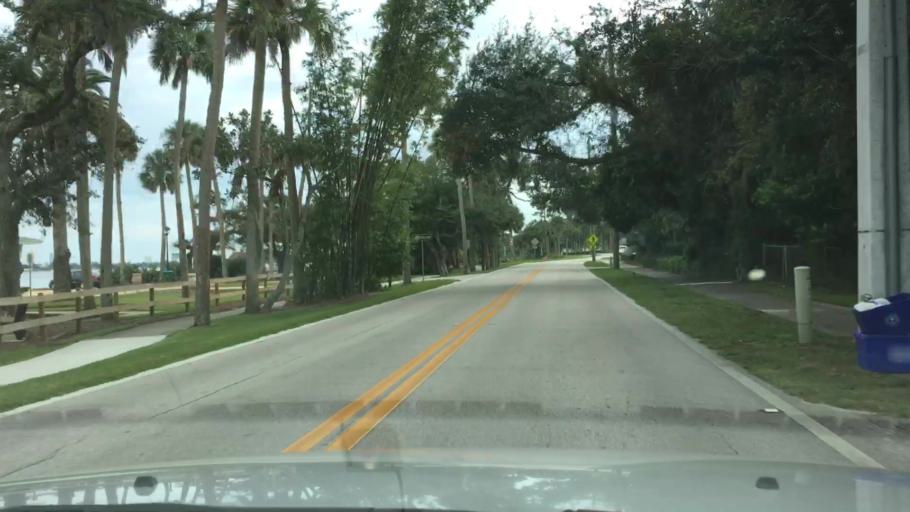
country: US
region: Florida
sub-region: Volusia County
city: Ormond Beach
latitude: 29.2811
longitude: -81.0535
